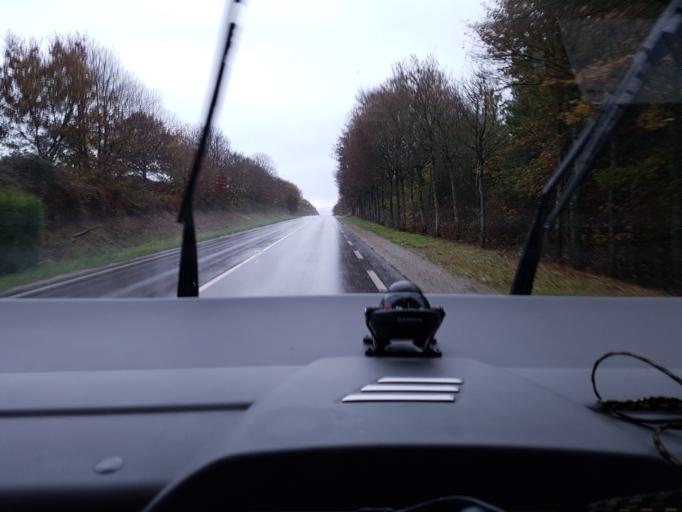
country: FR
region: Brittany
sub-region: Departement d'Ille-et-Vilaine
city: Vitre
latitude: 48.0964
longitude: -1.2060
